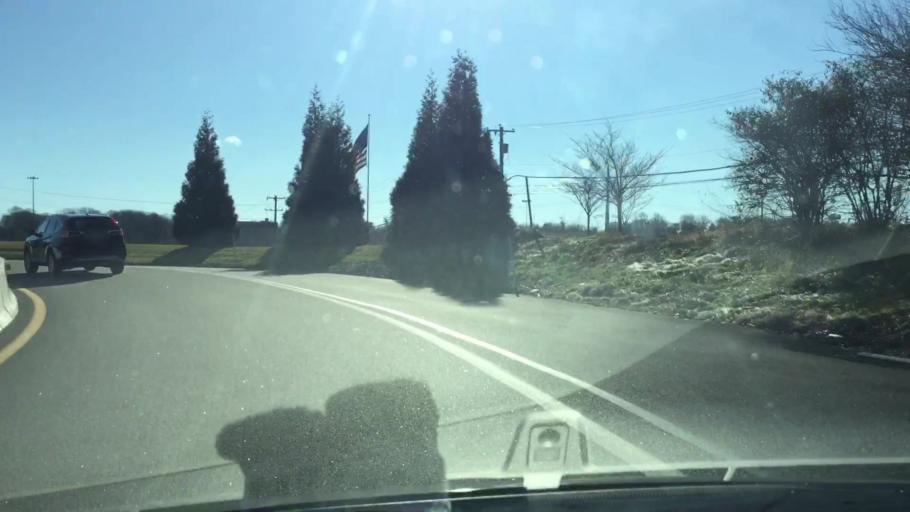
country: US
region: Pennsylvania
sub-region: Montgomery County
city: Horsham
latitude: 40.1642
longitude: -75.1259
